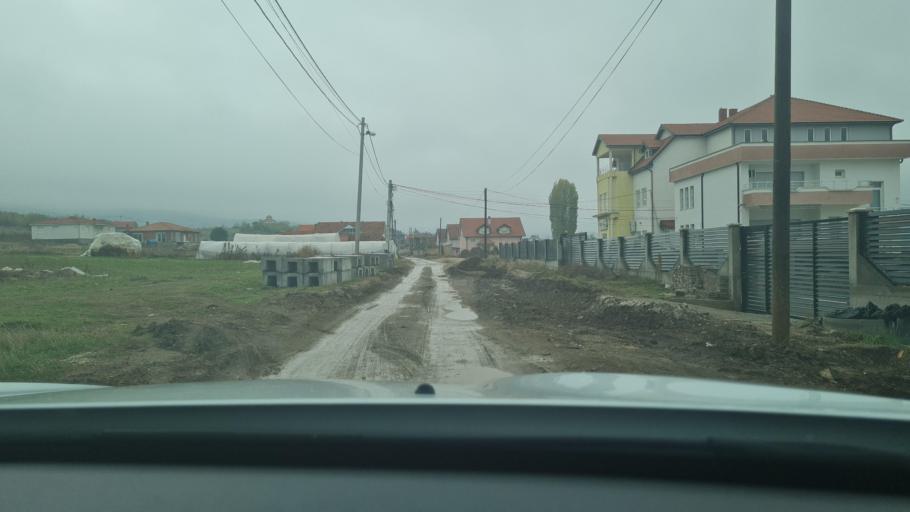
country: MK
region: Opstina Lipkovo
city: Matejche
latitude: 42.1187
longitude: 21.6050
